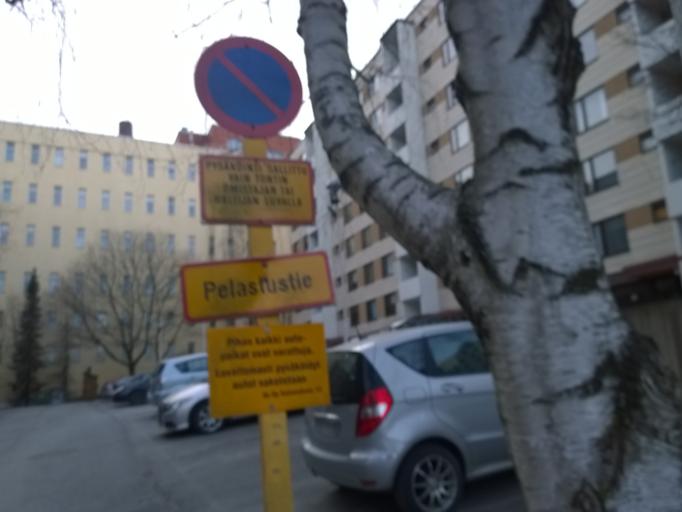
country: FI
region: Pirkanmaa
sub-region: Tampere
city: Tampere
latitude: 61.4942
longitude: 23.7504
